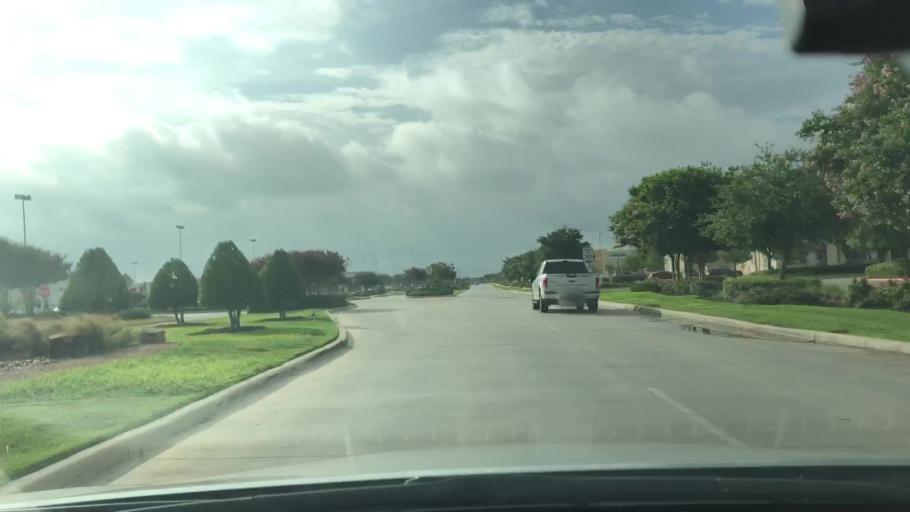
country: US
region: Texas
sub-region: Guadalupe County
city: Lake Dunlap
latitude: 29.7307
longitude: -98.0751
